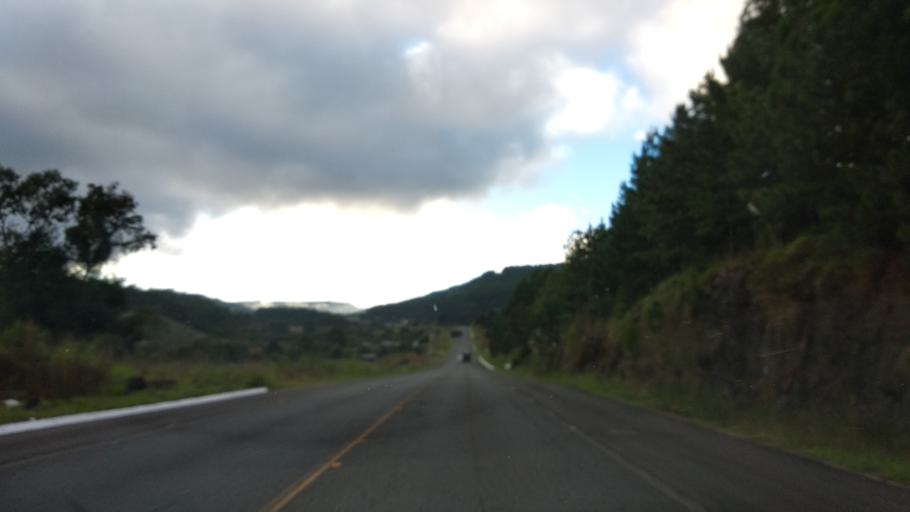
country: BR
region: Santa Catarina
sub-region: Curitibanos
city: Curitibanos
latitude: -27.5744
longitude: -50.7839
